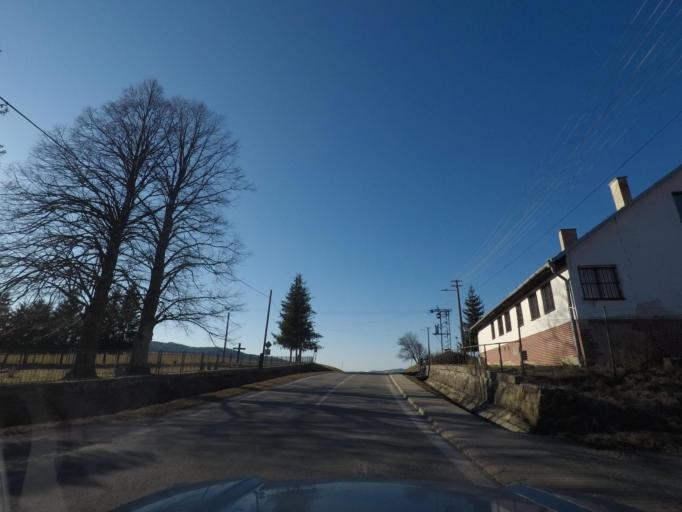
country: SK
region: Presovsky
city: Medzilaborce
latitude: 49.2232
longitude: 21.9729
